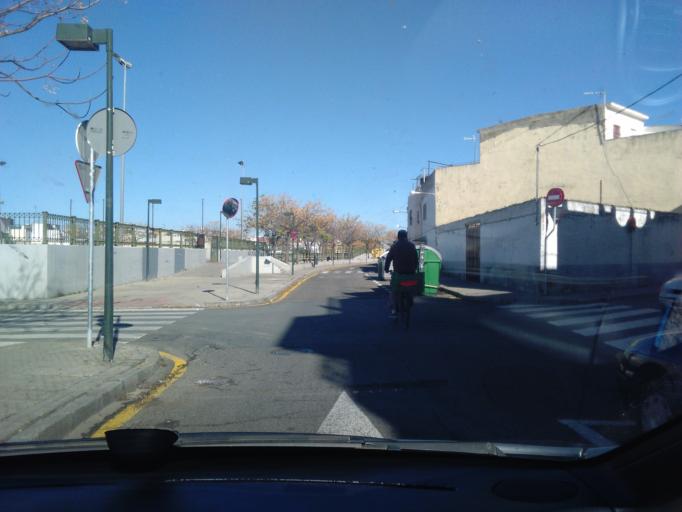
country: ES
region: Andalusia
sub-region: Provincia de Sevilla
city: Sevilla
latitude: 37.3872
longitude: -5.9087
